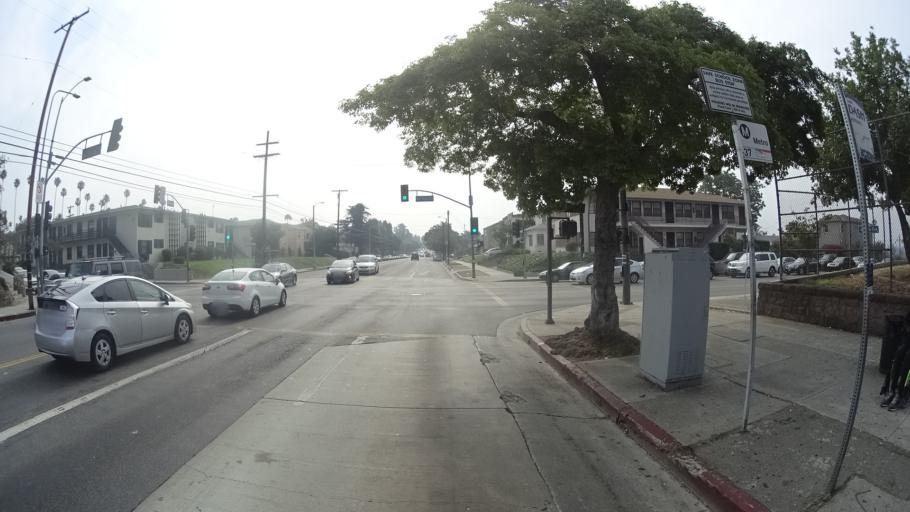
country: US
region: California
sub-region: Los Angeles County
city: View Park-Windsor Hills
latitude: 34.0326
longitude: -118.3180
